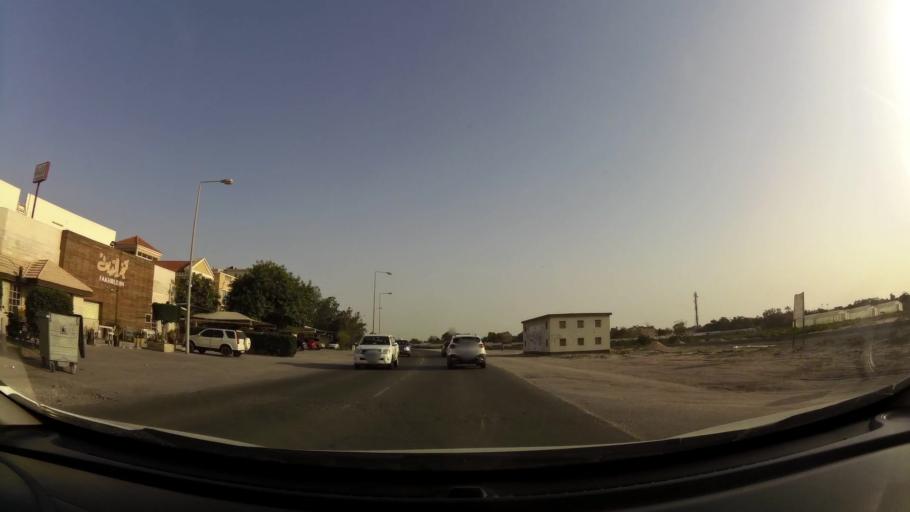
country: BH
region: Manama
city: Jidd Hafs
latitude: 26.2113
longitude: 50.4806
